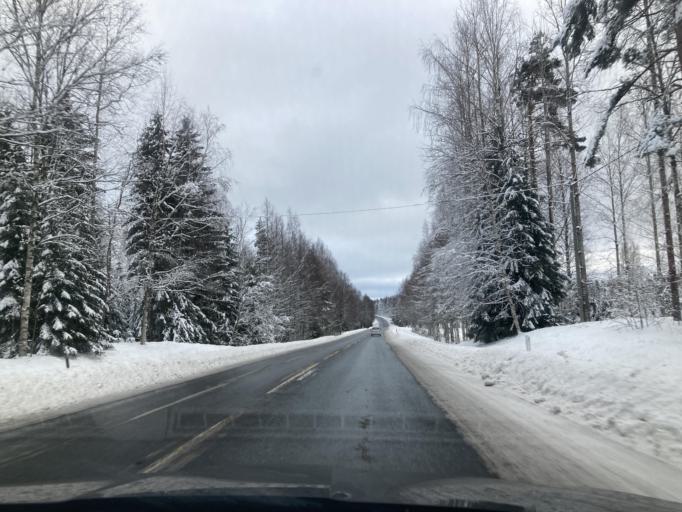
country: FI
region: Paijanne Tavastia
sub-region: Lahti
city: Padasjoki
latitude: 61.3025
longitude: 25.2982
